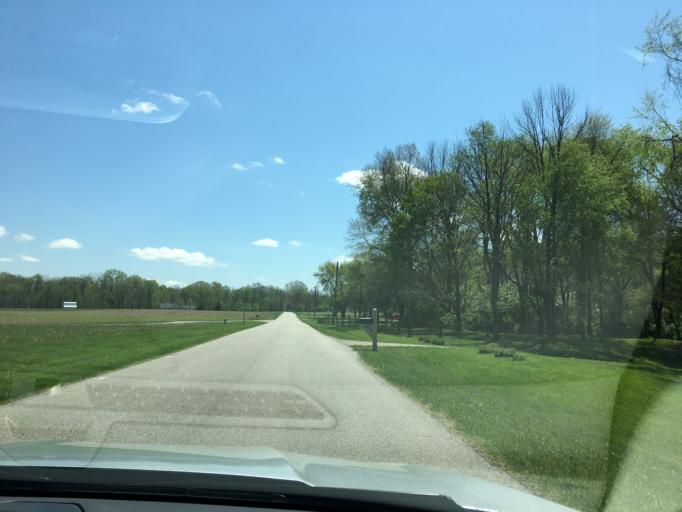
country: US
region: Indiana
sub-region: Tippecanoe County
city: Dayton
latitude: 40.3132
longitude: -86.7451
